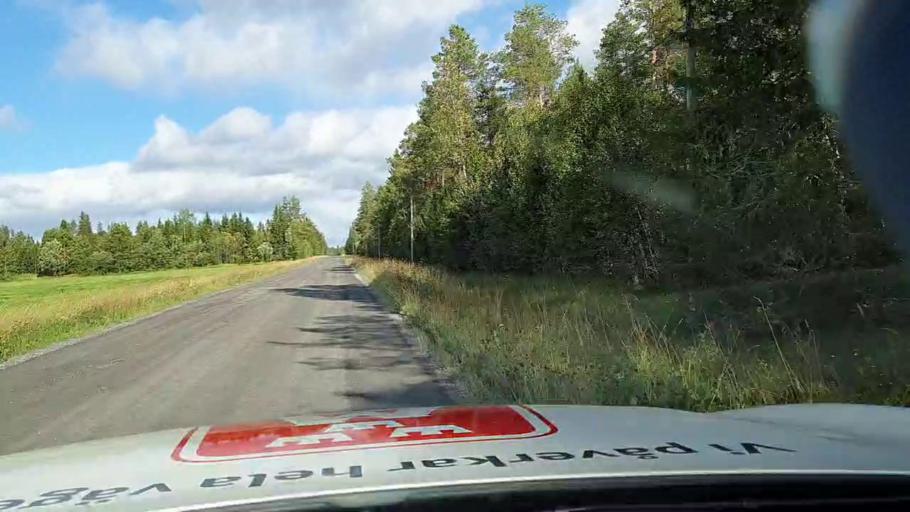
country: SE
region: Jaemtland
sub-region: Stroemsunds Kommun
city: Stroemsund
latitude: 63.6868
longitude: 15.1233
